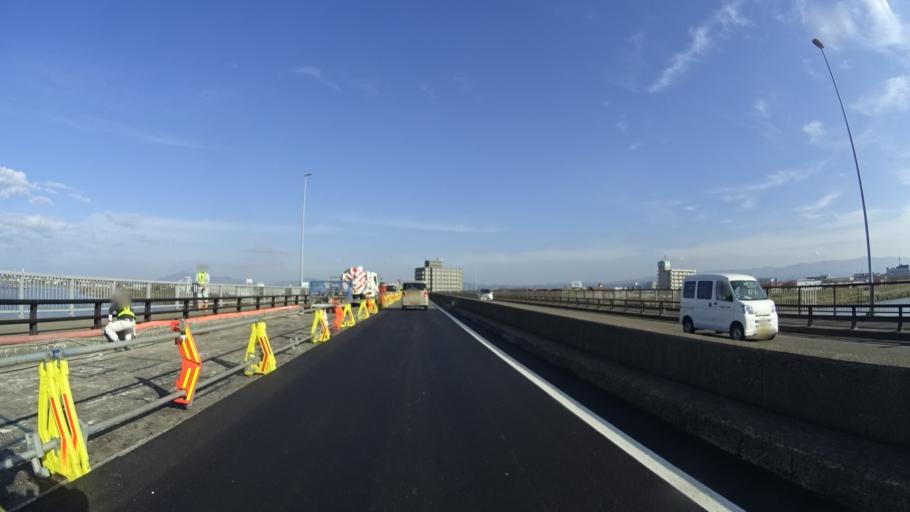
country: JP
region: Niigata
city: Joetsu
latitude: 37.1620
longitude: 138.2443
